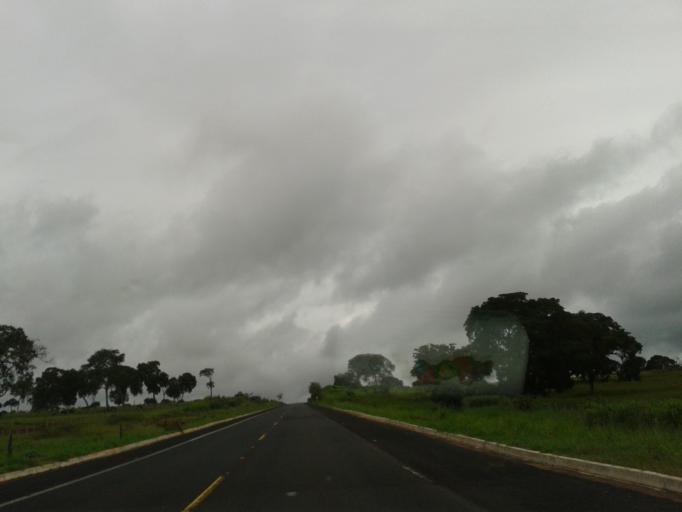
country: BR
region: Minas Gerais
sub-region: Santa Vitoria
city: Santa Vitoria
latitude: -19.2368
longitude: -50.0162
